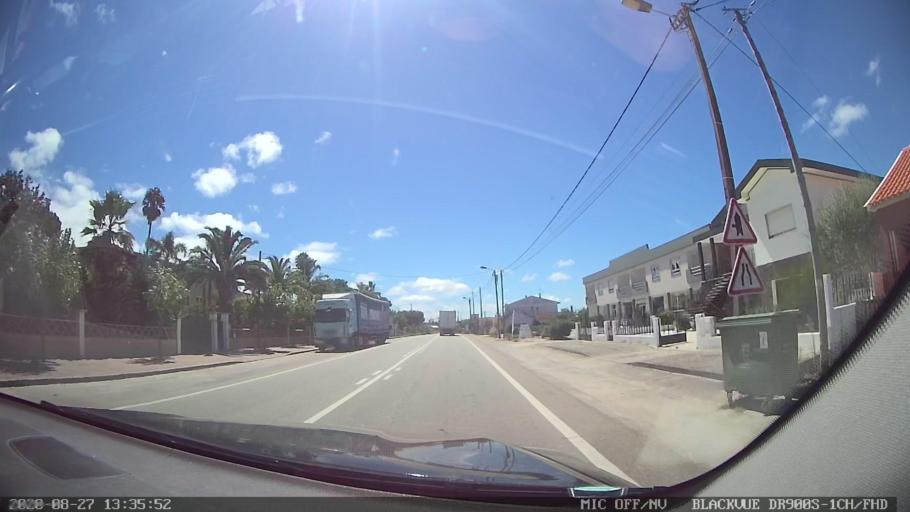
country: PT
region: Coimbra
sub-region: Mira
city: Mira
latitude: 40.4599
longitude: -8.7017
